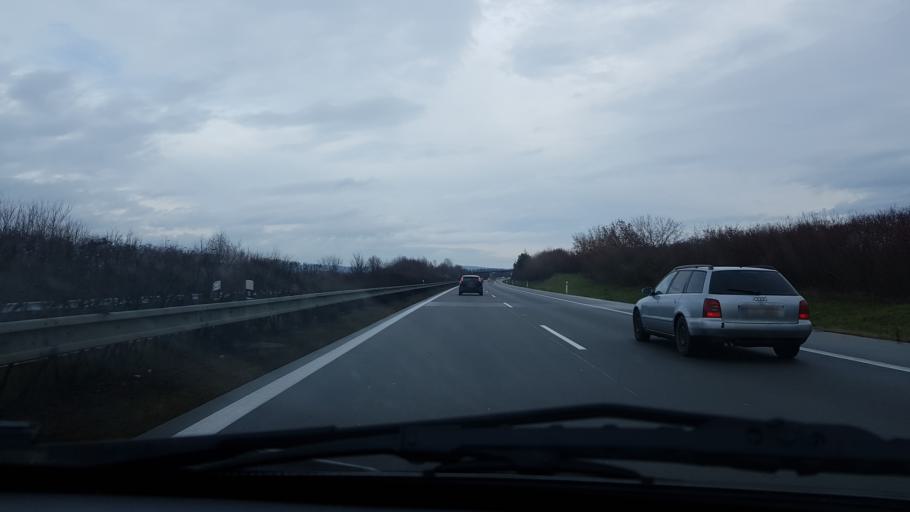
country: CZ
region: Olomoucky
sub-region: Okres Olomouc
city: Velka Bystrice
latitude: 49.5747
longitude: 17.3594
